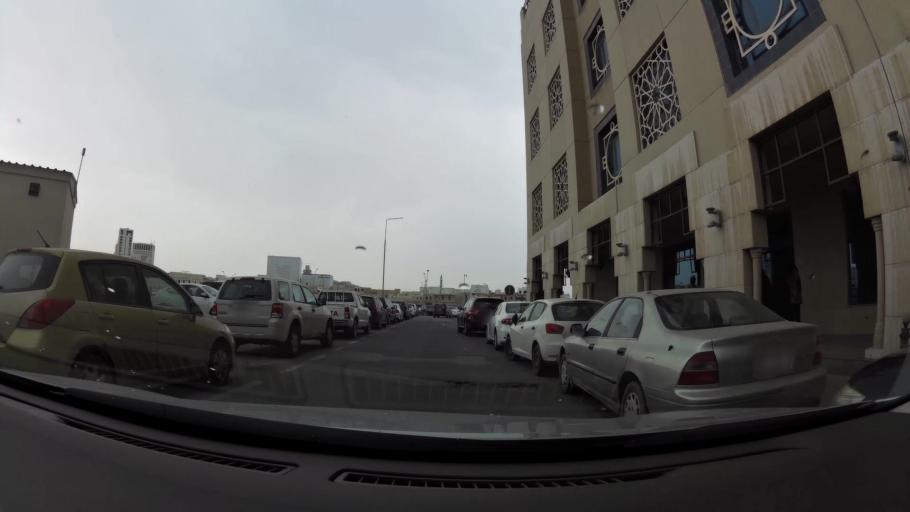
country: QA
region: Baladiyat ad Dawhah
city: Doha
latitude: 25.2886
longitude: 51.5360
